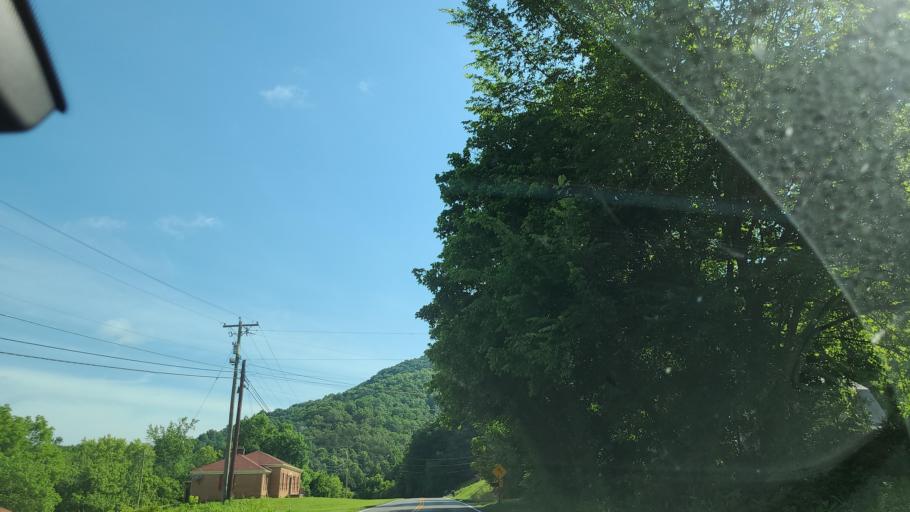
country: US
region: Kentucky
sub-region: Bell County
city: Pineville
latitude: 36.7683
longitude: -83.7726
